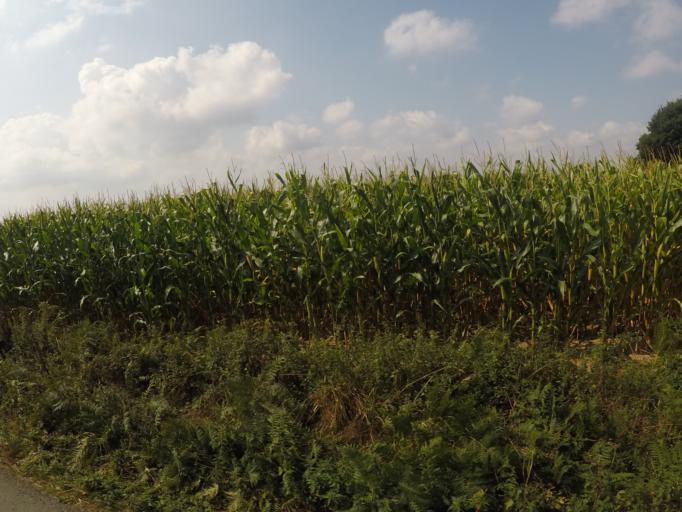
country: FR
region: Brittany
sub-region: Departement des Cotes-d'Armor
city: Tremuson
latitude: 48.5526
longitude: -2.8923
